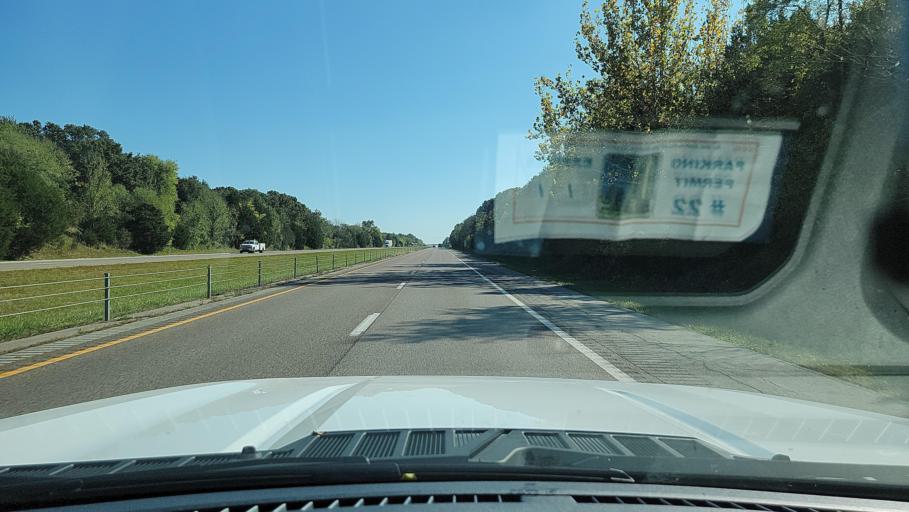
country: US
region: Missouri
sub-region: Jefferson County
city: Crystal City
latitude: 38.1223
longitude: -90.3107
